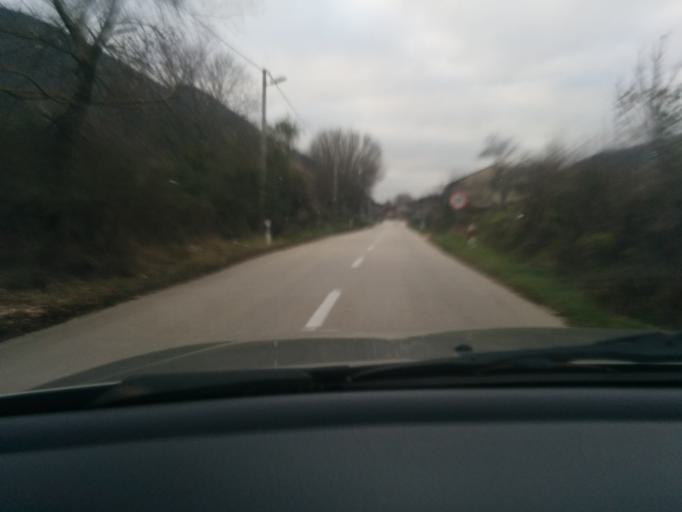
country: HR
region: Splitsko-Dalmatinska
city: Sinj
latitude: 43.7125
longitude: 16.5822
